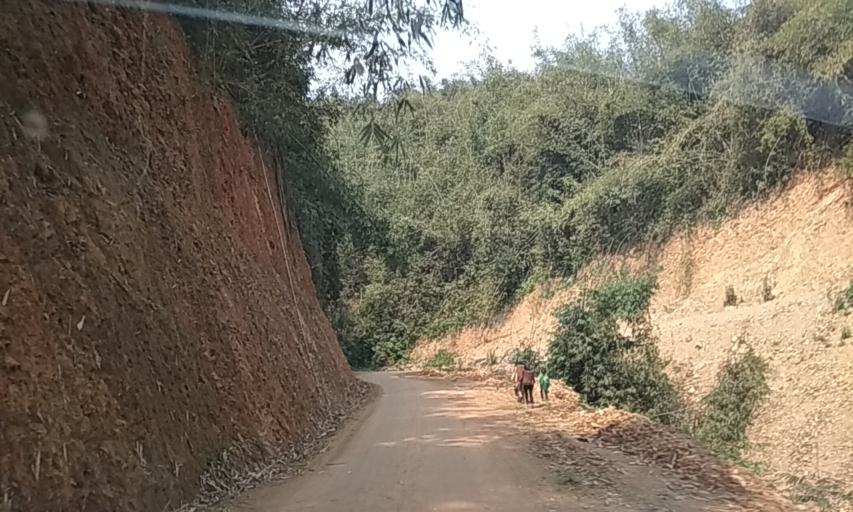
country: LA
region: Phongsali
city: Phongsali
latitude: 21.4702
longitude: 102.4296
